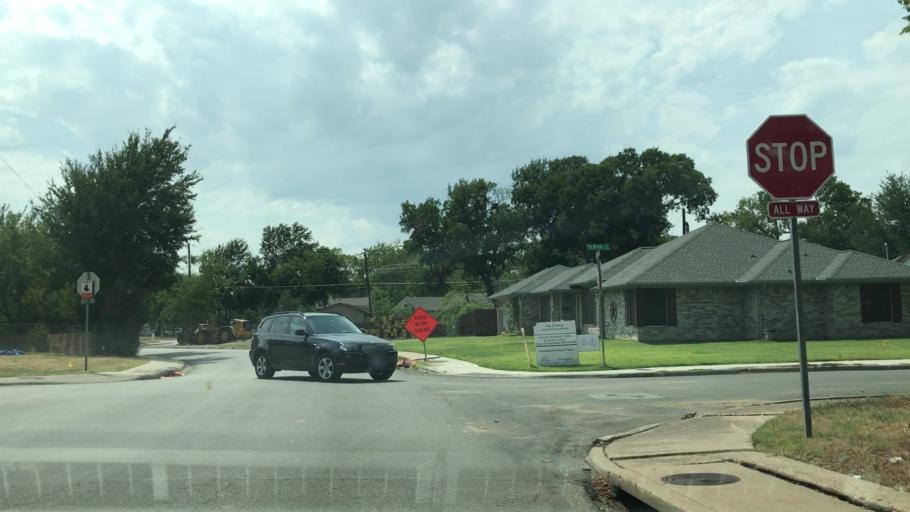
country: US
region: Texas
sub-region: Dallas County
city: Irving
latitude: 32.8404
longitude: -96.9478
